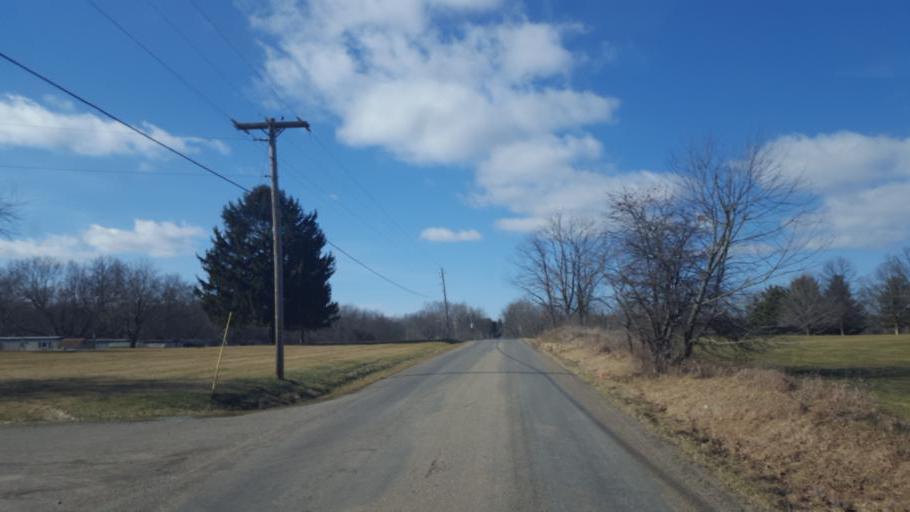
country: US
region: Ohio
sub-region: Richland County
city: Lexington
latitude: 40.6374
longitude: -82.6112
